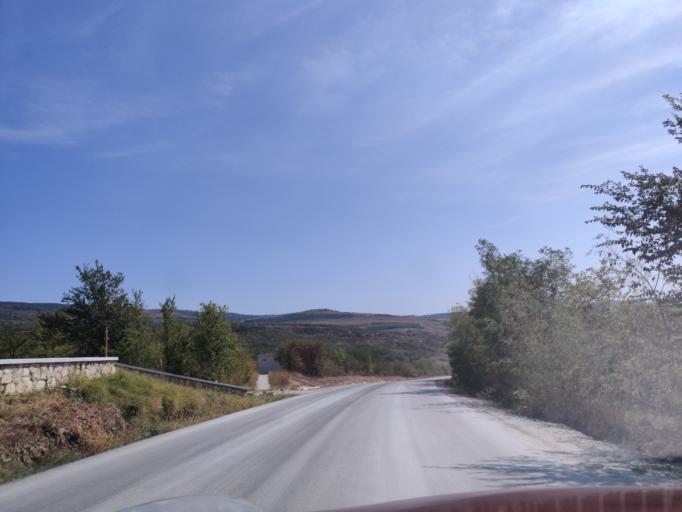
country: MD
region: Ungheni
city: Ungheni
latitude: 47.2562
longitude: 27.9954
